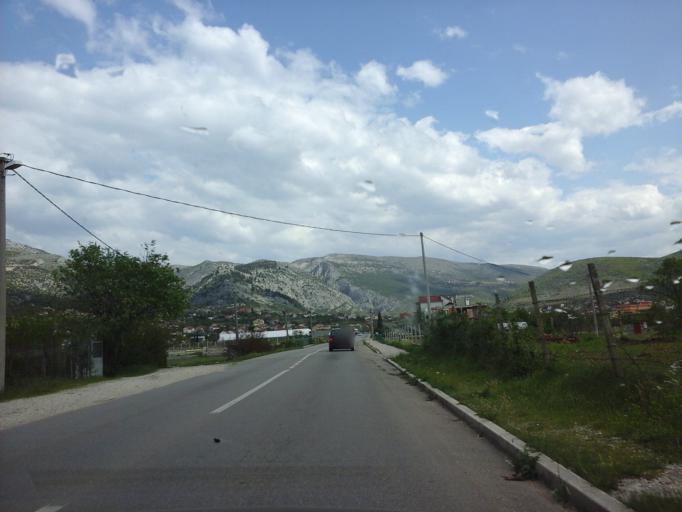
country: BA
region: Federation of Bosnia and Herzegovina
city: Blagaj
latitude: 43.2658
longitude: 17.8734
